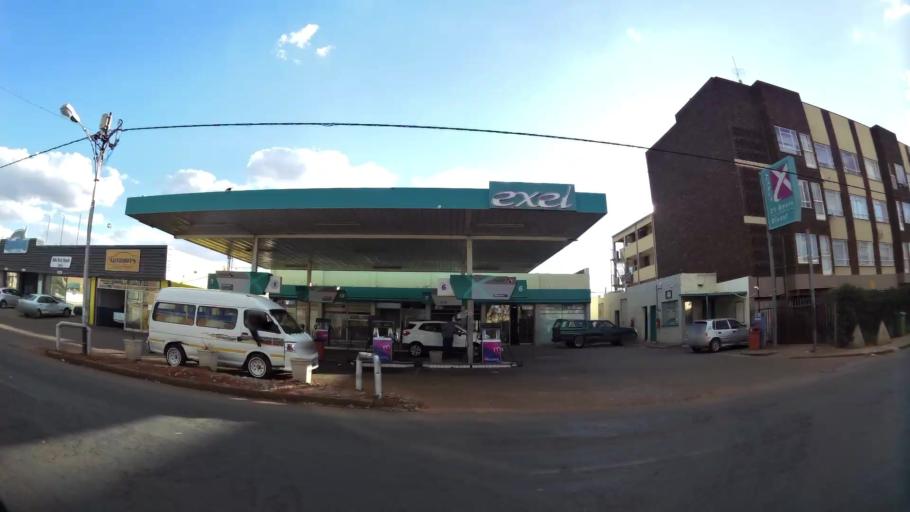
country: ZA
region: North-West
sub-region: Dr Kenneth Kaunda District Municipality
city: Potchefstroom
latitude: -26.7052
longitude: 27.0978
